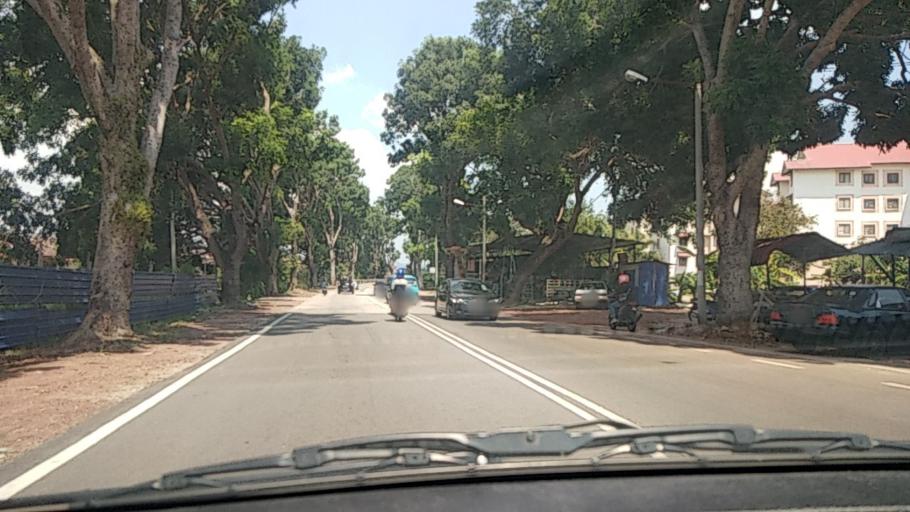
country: MY
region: Kedah
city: Sungai Petani
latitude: 5.6430
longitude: 100.5171
